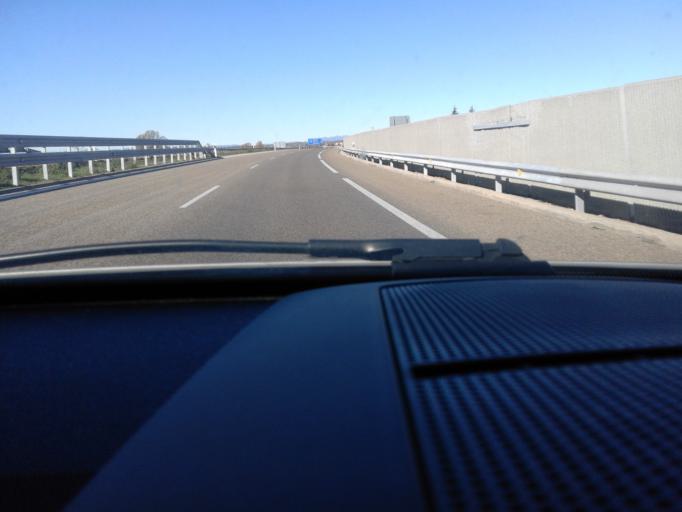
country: ES
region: Castille and Leon
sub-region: Provincia de Leon
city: Valverde de la Virgen
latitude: 42.5580
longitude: -5.6353
